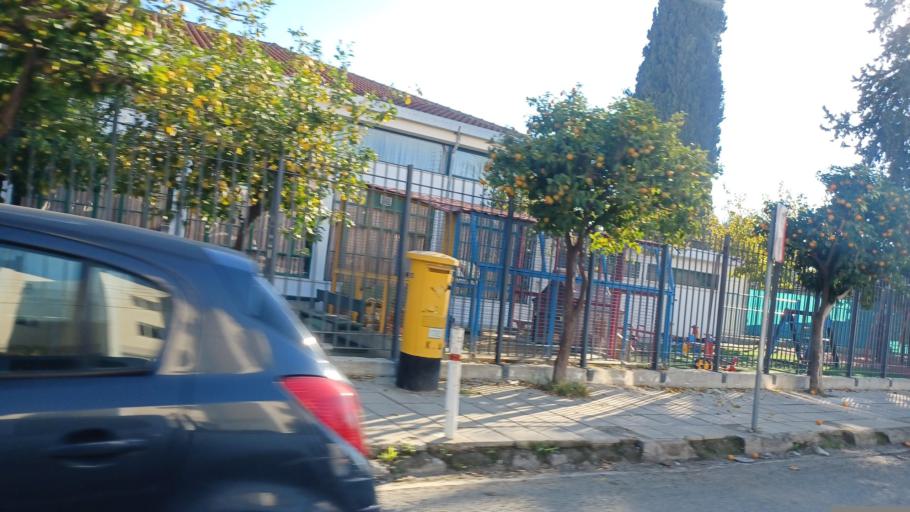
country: CY
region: Lefkosia
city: Nicosia
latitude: 35.1498
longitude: 33.3398
